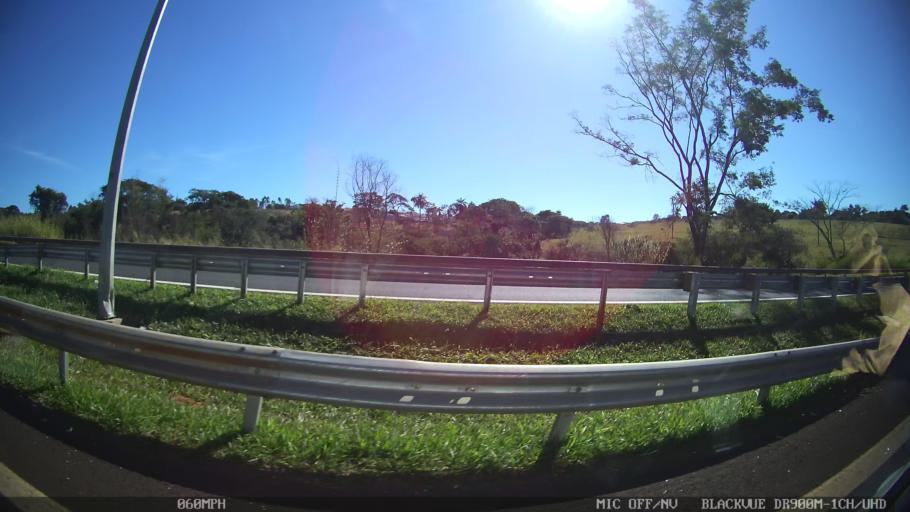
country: BR
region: Sao Paulo
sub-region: Franca
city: Franca
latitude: -20.5758
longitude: -47.3592
